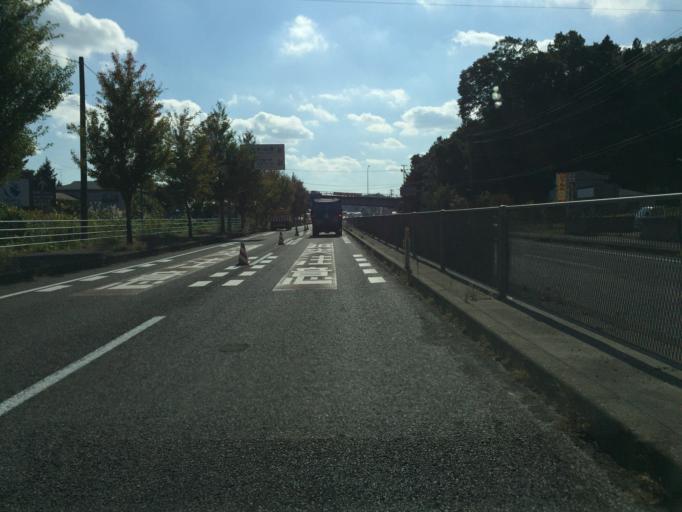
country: JP
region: Fukushima
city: Nihommatsu
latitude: 37.5970
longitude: 140.4599
